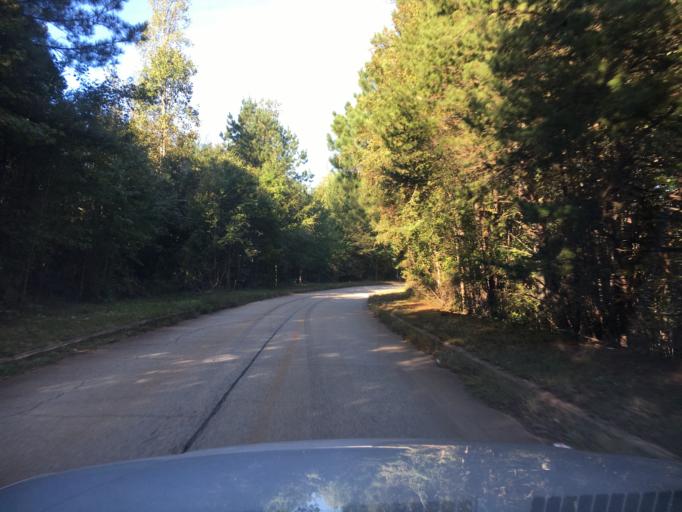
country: US
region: South Carolina
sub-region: Spartanburg County
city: Wellford
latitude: 34.9103
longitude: -82.0905
